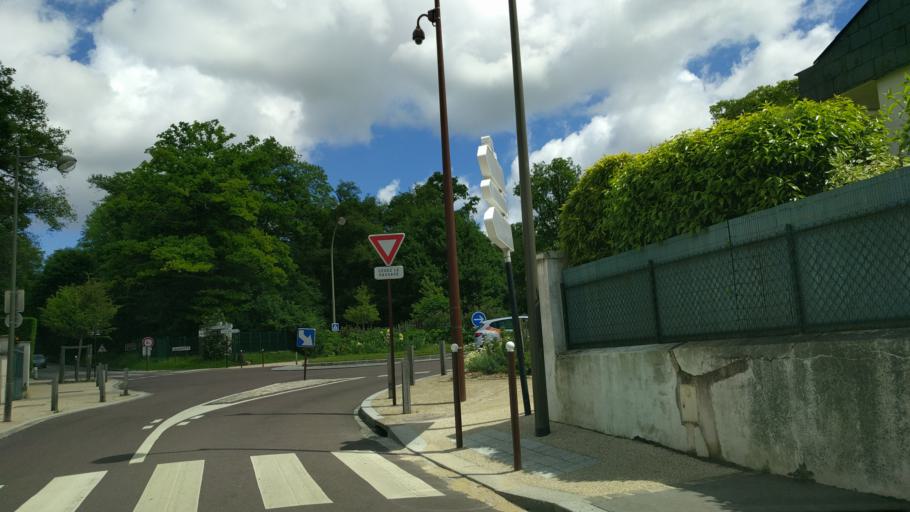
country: FR
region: Ile-de-France
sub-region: Departement des Yvelines
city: Le Chesnay
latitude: 48.8254
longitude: 2.1425
